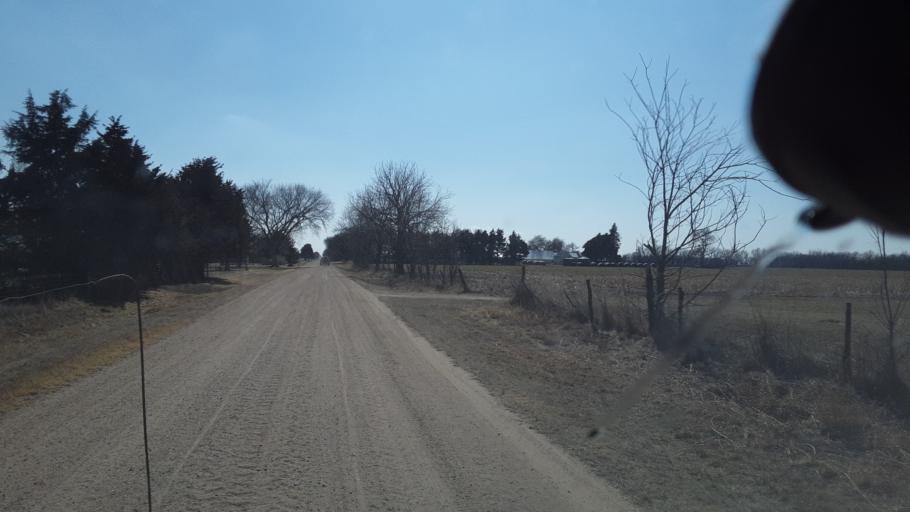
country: US
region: Kansas
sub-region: Reno County
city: Haven
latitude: 37.9180
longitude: -97.8484
